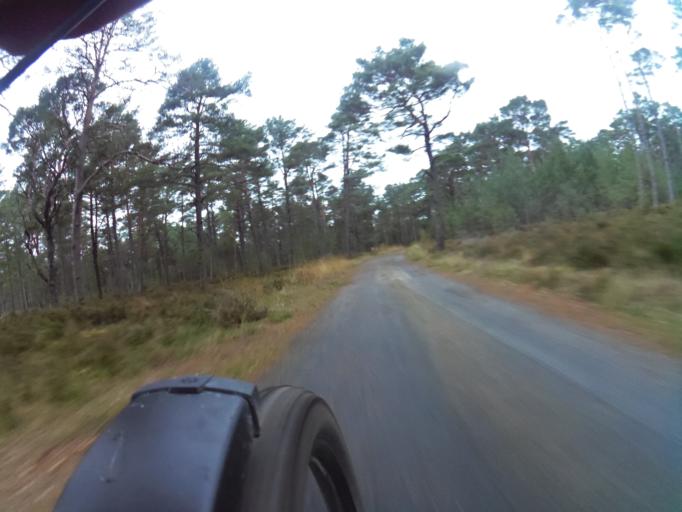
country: PL
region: Pomeranian Voivodeship
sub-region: Powiat wejherowski
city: Choczewo
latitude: 54.7926
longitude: 17.7596
